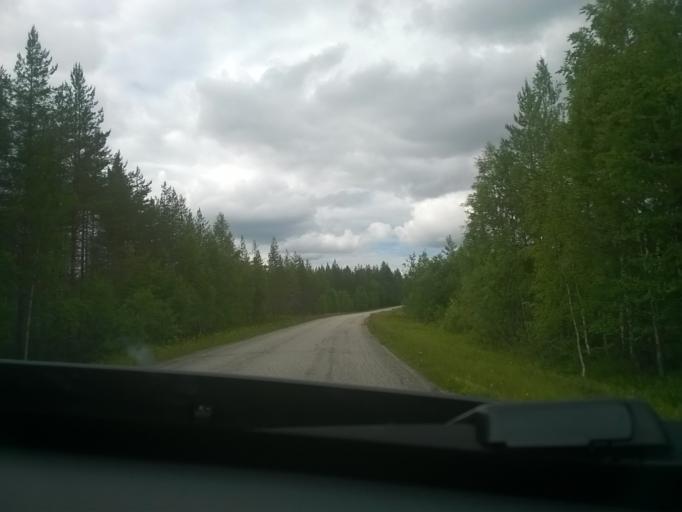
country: FI
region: Kainuu
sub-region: Kehys-Kainuu
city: Kuhmo
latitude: 64.3878
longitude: 29.7907
